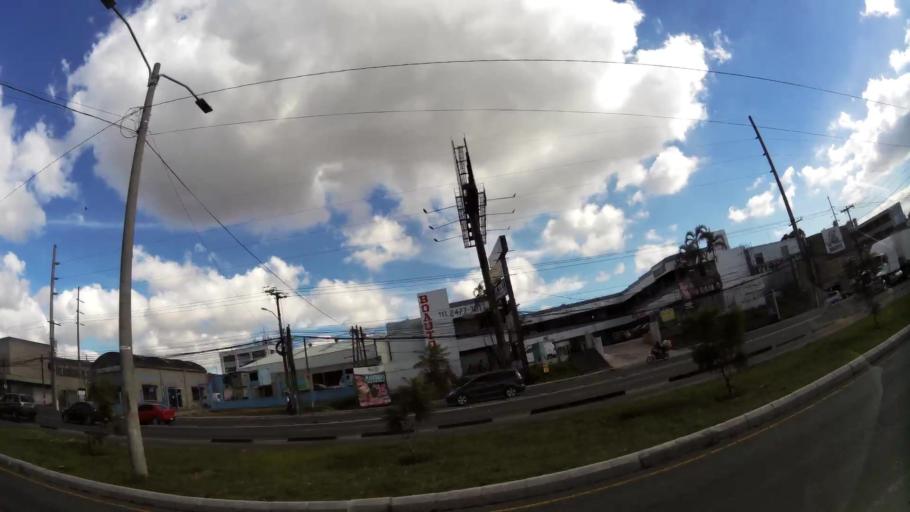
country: GT
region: Guatemala
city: Villa Nueva
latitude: 14.5817
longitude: -90.5673
